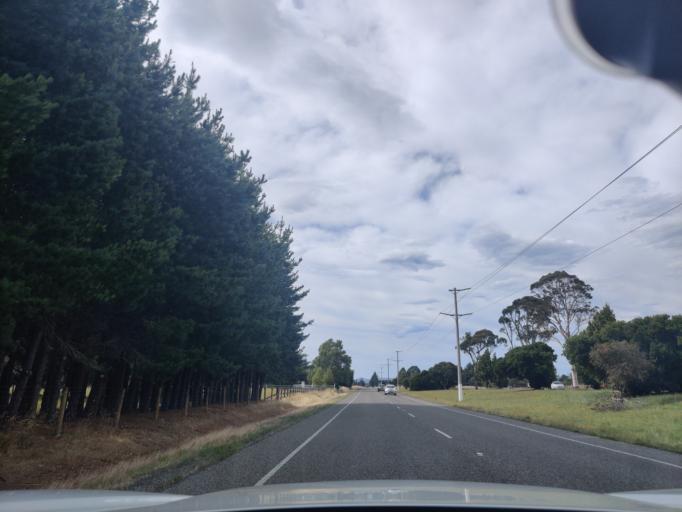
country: NZ
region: Wellington
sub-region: Masterton District
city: Masterton
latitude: -40.8466
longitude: 175.6337
